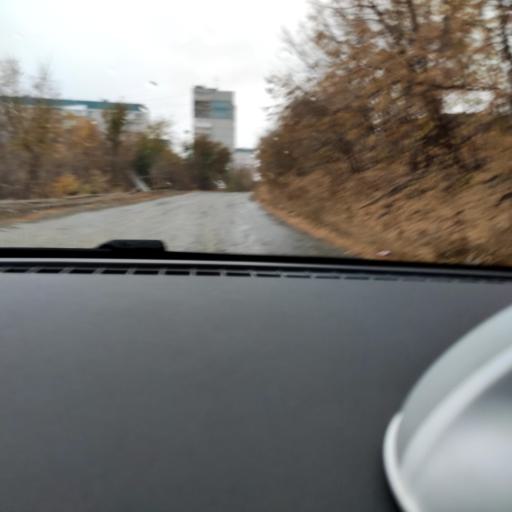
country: RU
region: Samara
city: Samara
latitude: 53.1909
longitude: 50.1527
